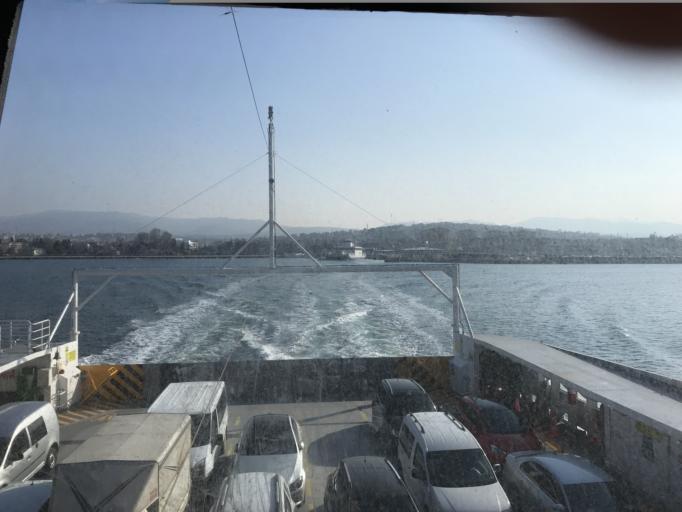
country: TR
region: Yalova
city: Yalova
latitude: 40.6654
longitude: 29.2786
